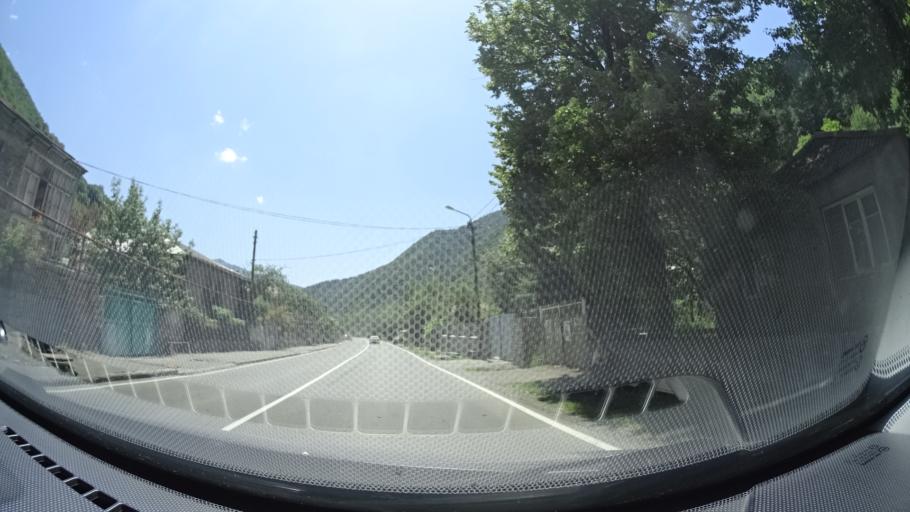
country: GE
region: Mtskheta-Mtianeti
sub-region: Dusheti
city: P'asanauri
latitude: 42.3621
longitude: 44.6848
